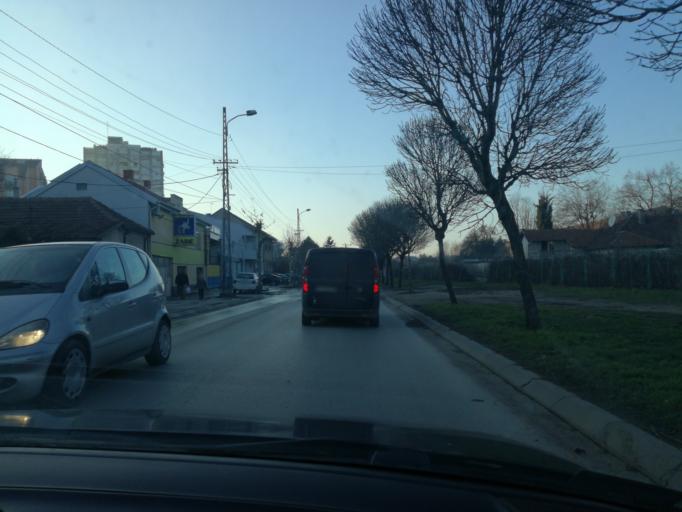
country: RS
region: Central Serbia
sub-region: Nisavski Okrug
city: Nis
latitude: 43.3123
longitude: 21.8905
